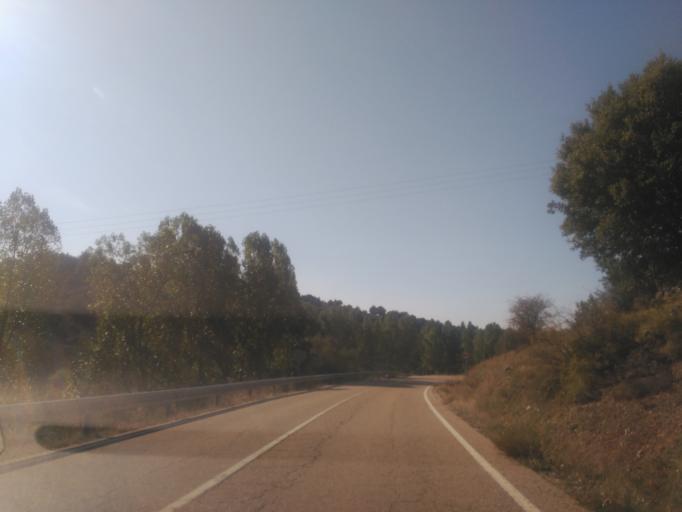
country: ES
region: Castille and Leon
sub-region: Provincia de Soria
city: Casarejos
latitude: 41.7931
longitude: -3.0290
